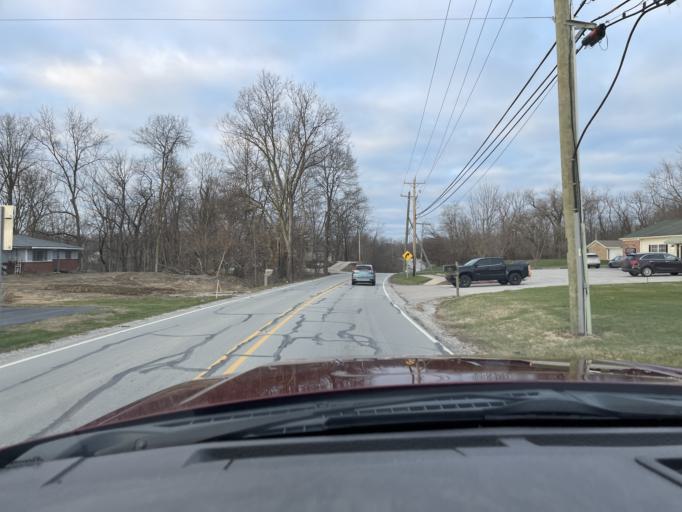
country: US
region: Indiana
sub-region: Hendricks County
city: Avon
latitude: 39.7657
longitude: -86.4001
